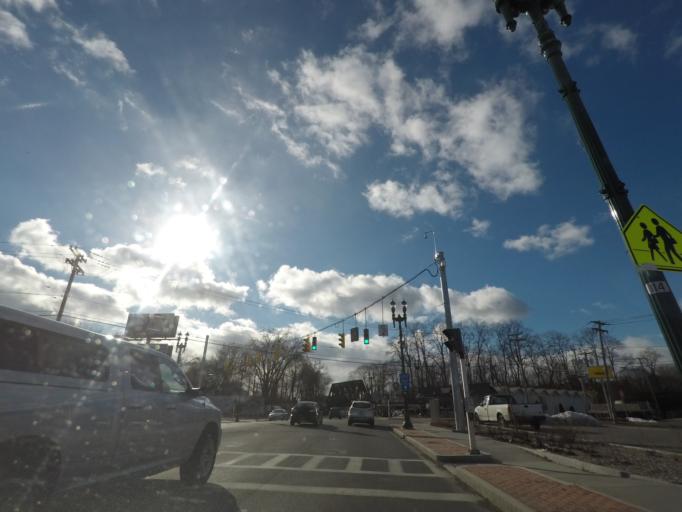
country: US
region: New York
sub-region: Schenectady County
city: Schenectady
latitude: 42.8183
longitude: -73.9399
